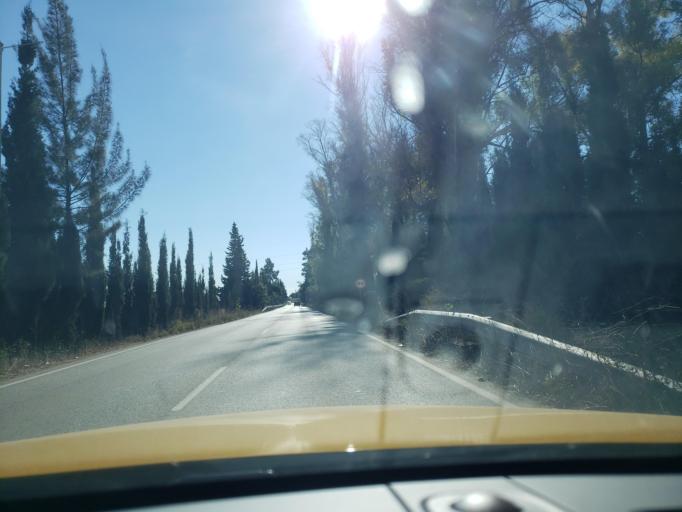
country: ES
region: Andalusia
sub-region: Provincia de Malaga
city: Benahavis
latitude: 36.4817
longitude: -5.0147
